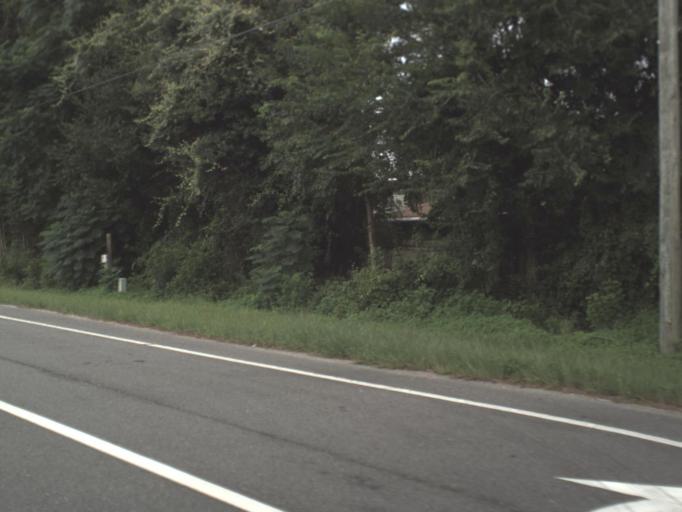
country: US
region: Florida
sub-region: Hernando County
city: Ridge Manor
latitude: 28.5197
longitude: -82.1675
